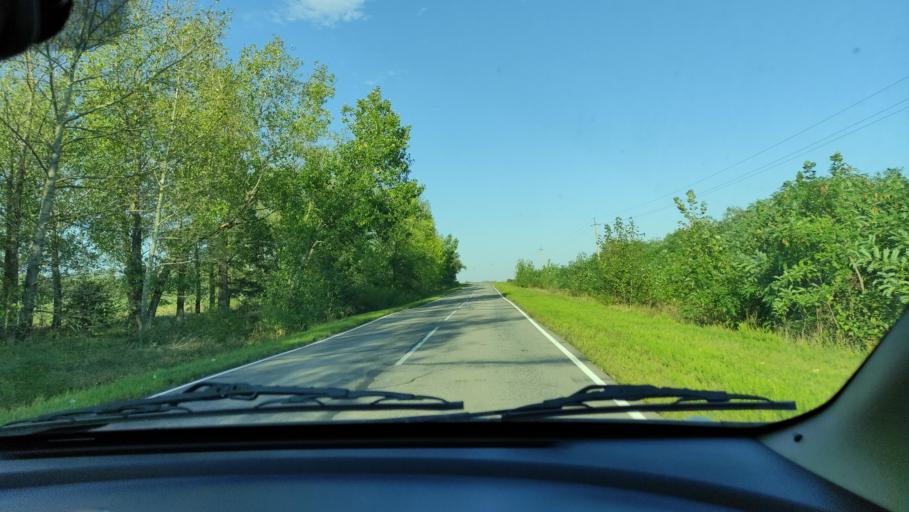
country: RU
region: Voronezj
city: Verkhniy Mamon
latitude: 50.1223
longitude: 40.3068
